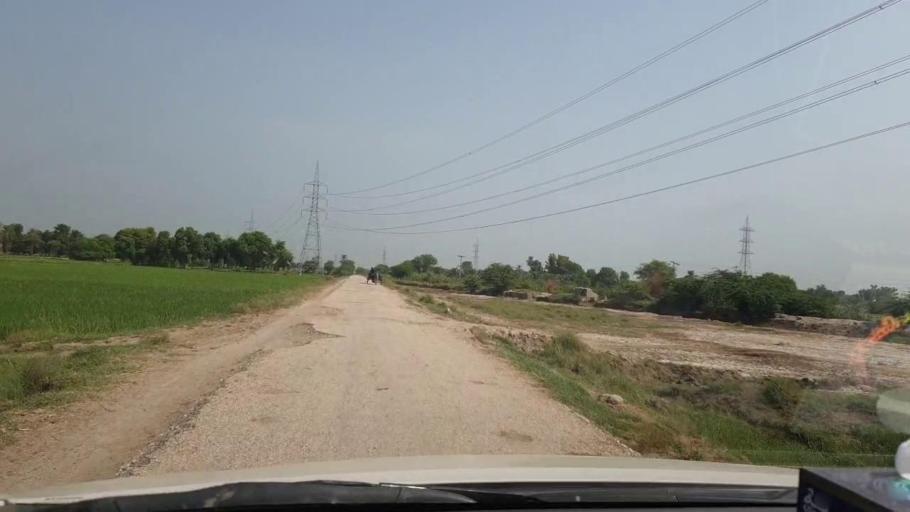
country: PK
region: Sindh
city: Shikarpur
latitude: 27.9766
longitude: 68.6645
